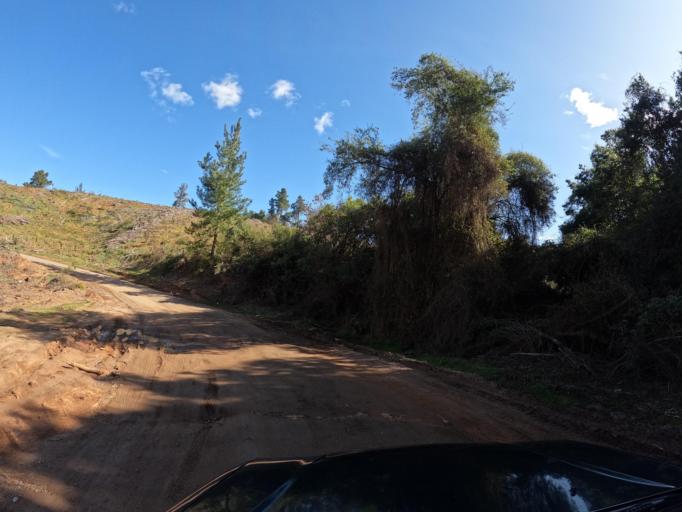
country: CL
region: Biobio
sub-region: Provincia de Biobio
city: La Laja
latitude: -37.0799
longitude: -72.8369
